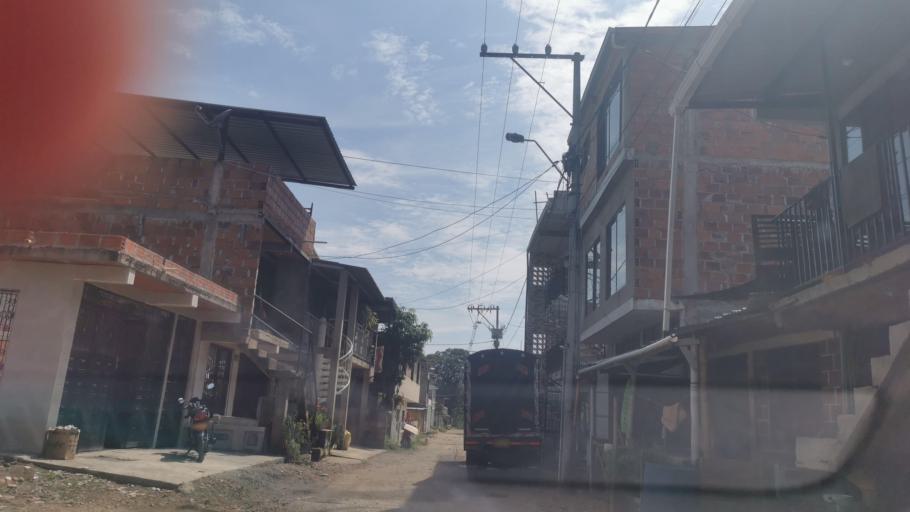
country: CO
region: Valle del Cauca
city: Jamundi
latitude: 3.2628
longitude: -76.5309
